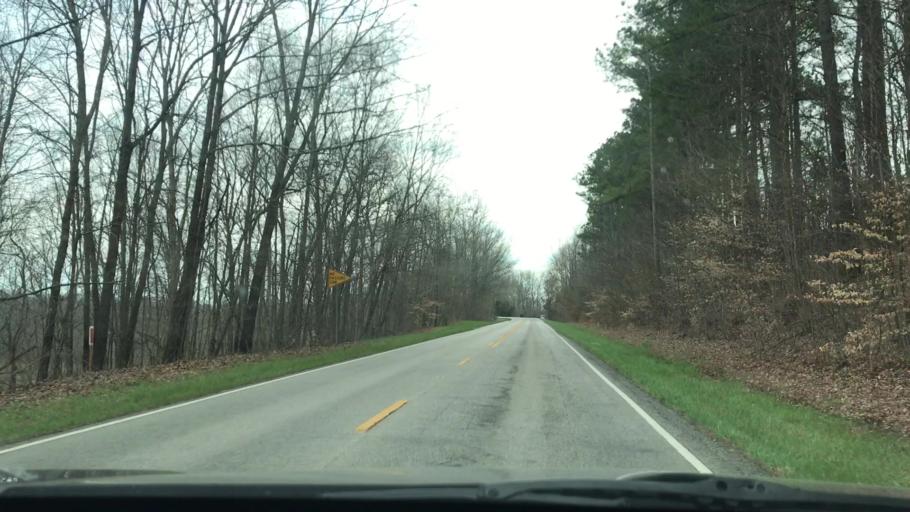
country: US
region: Kentucky
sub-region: Hart County
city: Munfordville
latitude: 37.3069
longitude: -85.7635
